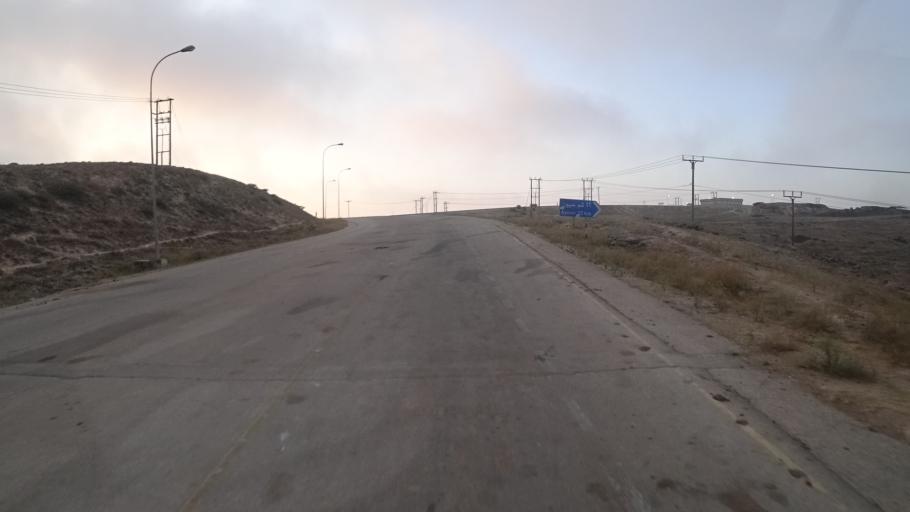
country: OM
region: Zufar
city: Salalah
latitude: 17.1218
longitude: 53.9281
